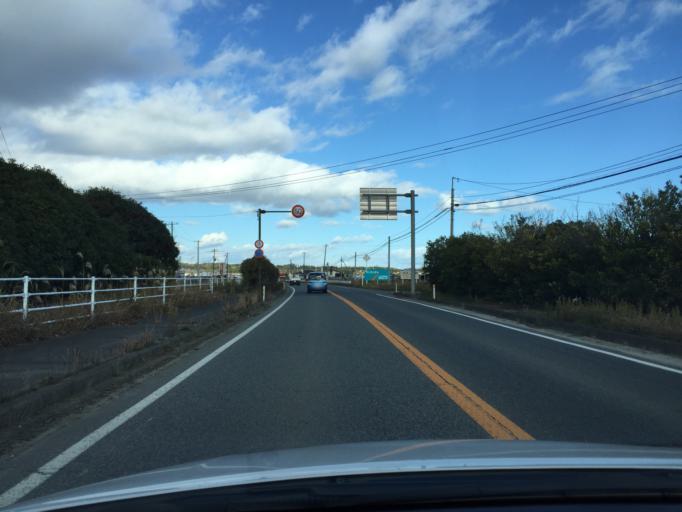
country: JP
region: Fukushima
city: Namie
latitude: 37.5518
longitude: 141.0061
